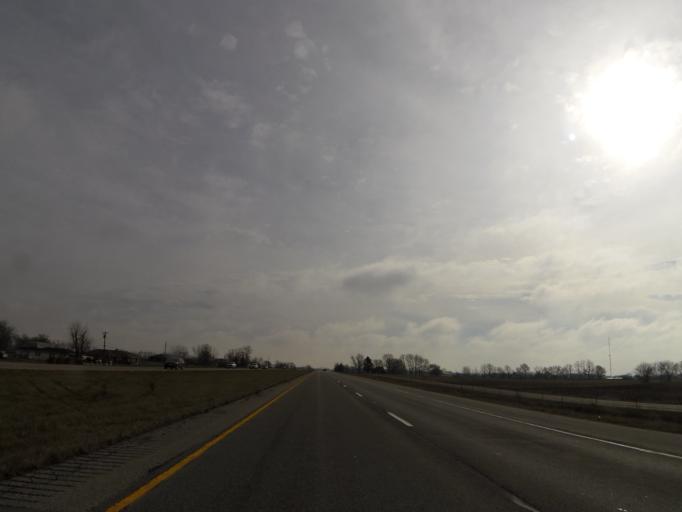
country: US
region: Indiana
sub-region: Hancock County
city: New Palestine
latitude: 39.6219
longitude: -85.8755
